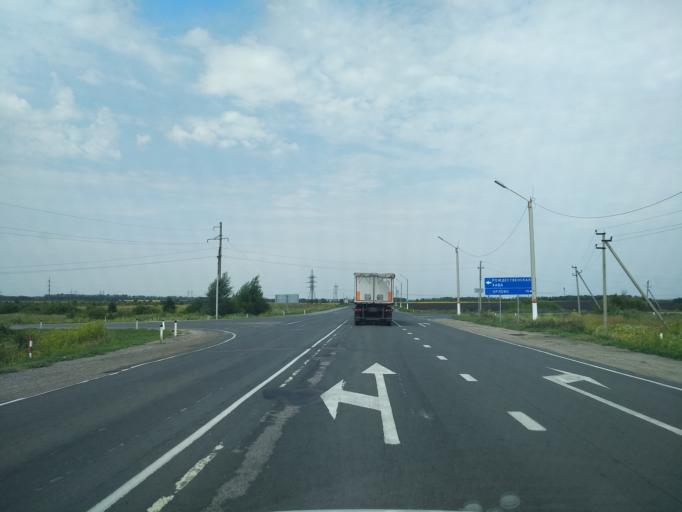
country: RU
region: Voronezj
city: Orlovo
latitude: 51.6778
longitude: 39.6812
